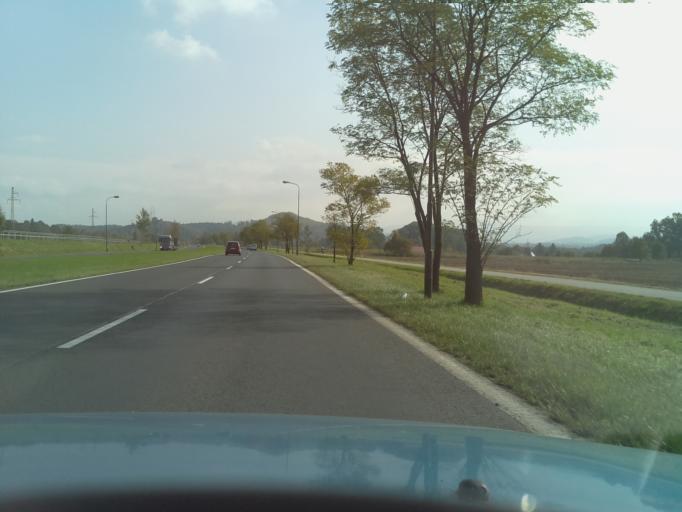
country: PL
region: Lower Silesian Voivodeship
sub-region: Powiat jeleniogorski
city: Jezow Sudecki
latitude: 50.9140
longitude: 15.7777
